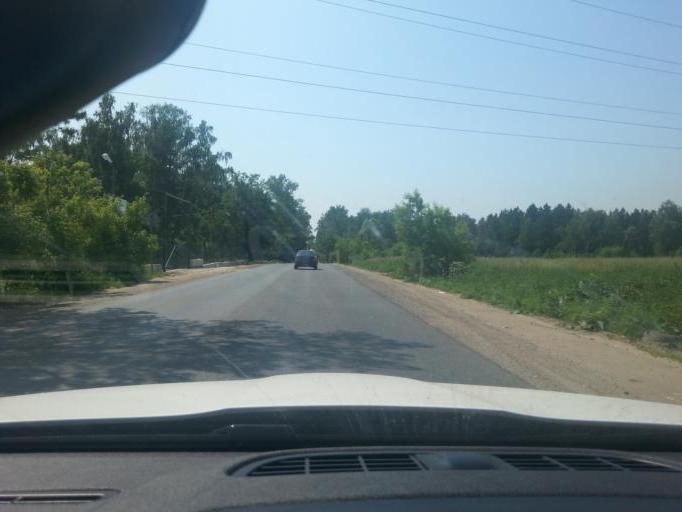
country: RU
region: Moskovskaya
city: Zheleznodorozhnyy
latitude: 55.7213
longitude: 37.9738
